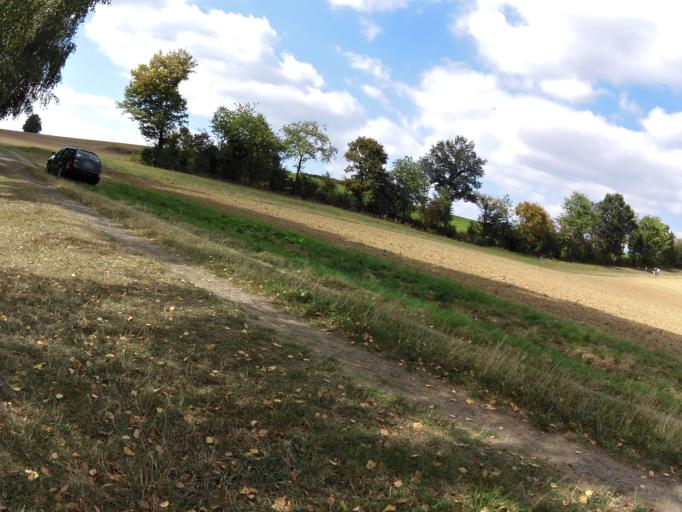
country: DE
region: Bavaria
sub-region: Regierungsbezirk Unterfranken
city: Hettstadt
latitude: 49.7909
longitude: 9.8262
